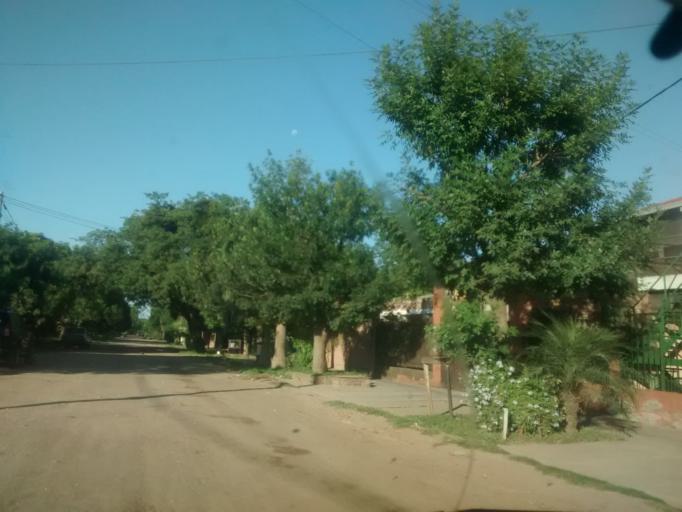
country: AR
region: Chaco
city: Resistencia
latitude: -27.4333
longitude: -58.9915
